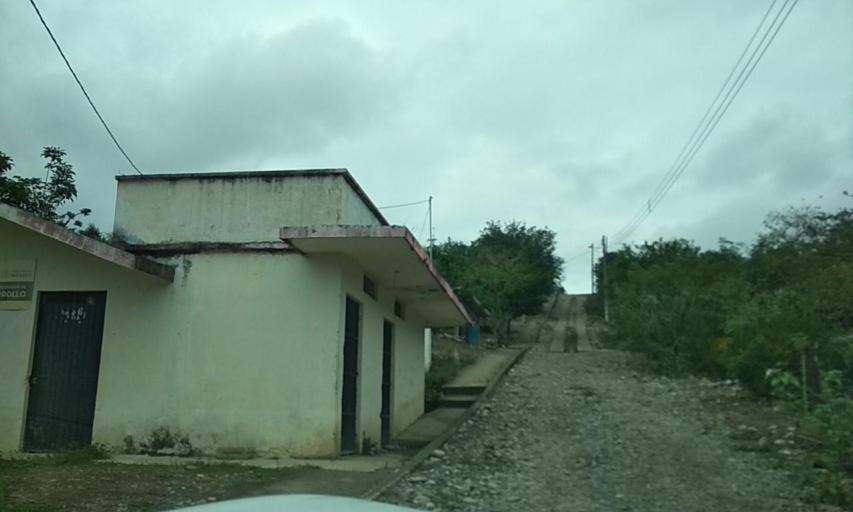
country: MX
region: Veracruz
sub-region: Coatzintla
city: Manuel Maria Contreras
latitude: 20.3409
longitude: -97.4652
